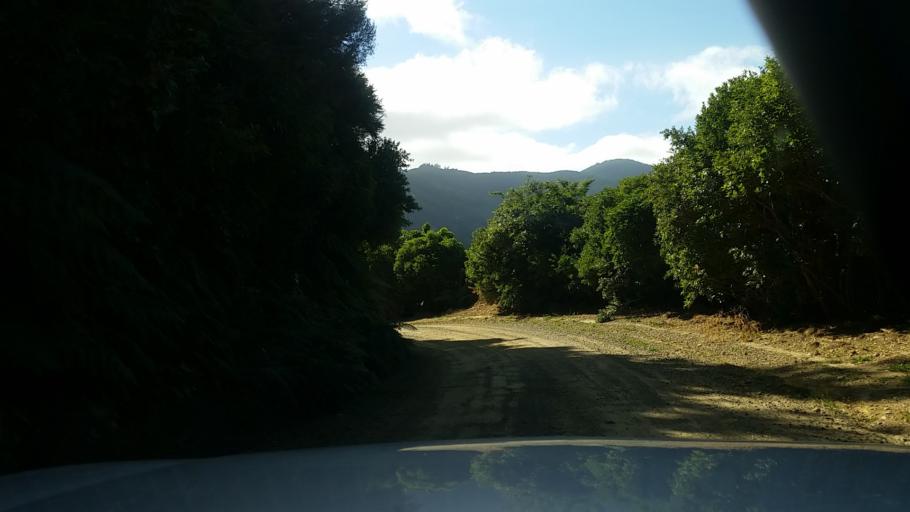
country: NZ
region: Marlborough
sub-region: Marlborough District
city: Picton
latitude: -41.2906
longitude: 174.1699
